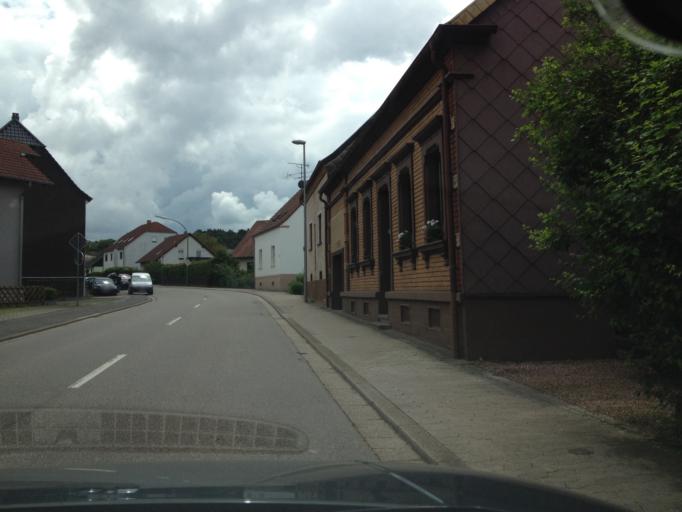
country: DE
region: Saarland
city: Bexbach
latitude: 49.3102
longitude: 7.2811
